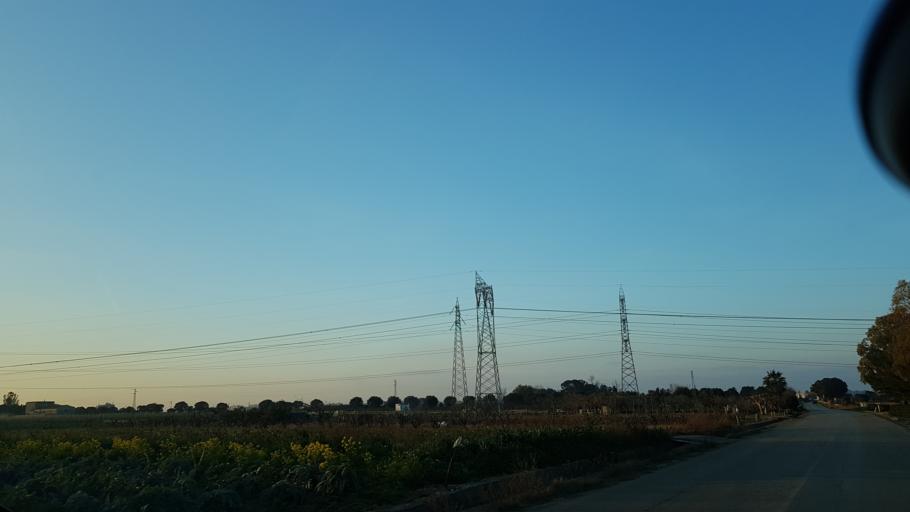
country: IT
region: Apulia
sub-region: Provincia di Brindisi
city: La Rosa
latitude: 40.5995
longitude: 17.9466
